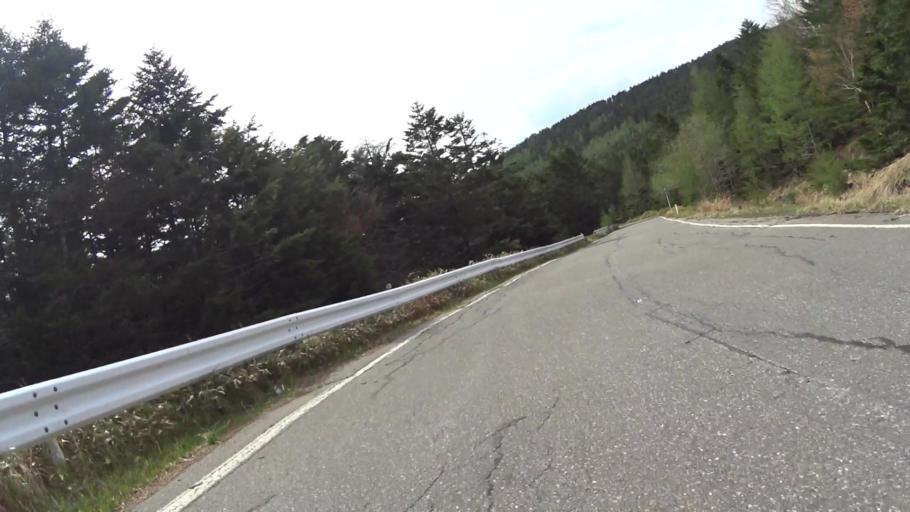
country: JP
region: Nagano
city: Chino
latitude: 36.0564
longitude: 138.3253
